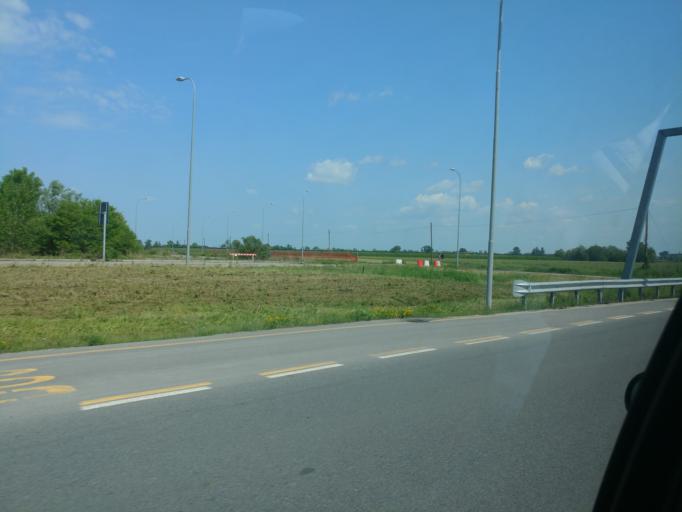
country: IT
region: Piedmont
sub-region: Provincia di Cuneo
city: Carde
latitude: 44.7334
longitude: 7.4225
